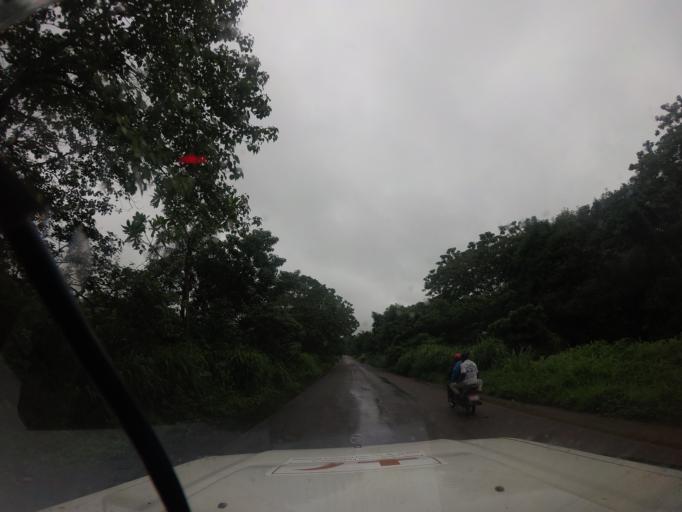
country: SL
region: Northern Province
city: Kabala
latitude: 9.5397
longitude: -11.5785
